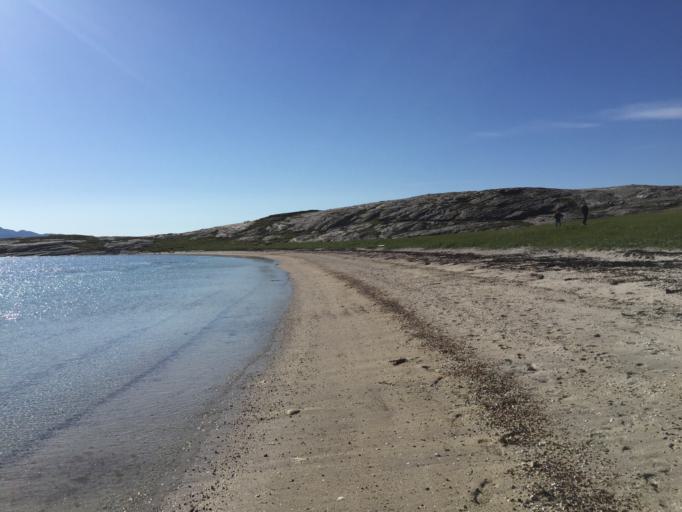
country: NO
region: Nordland
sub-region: Bodo
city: Loding
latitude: 67.4190
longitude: 14.6318
